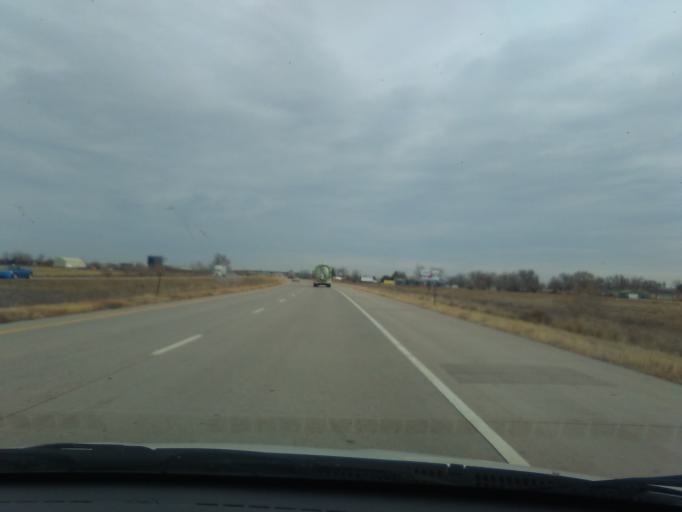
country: US
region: Colorado
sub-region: Morgan County
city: Fort Morgan
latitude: 40.2344
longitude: -104.0837
